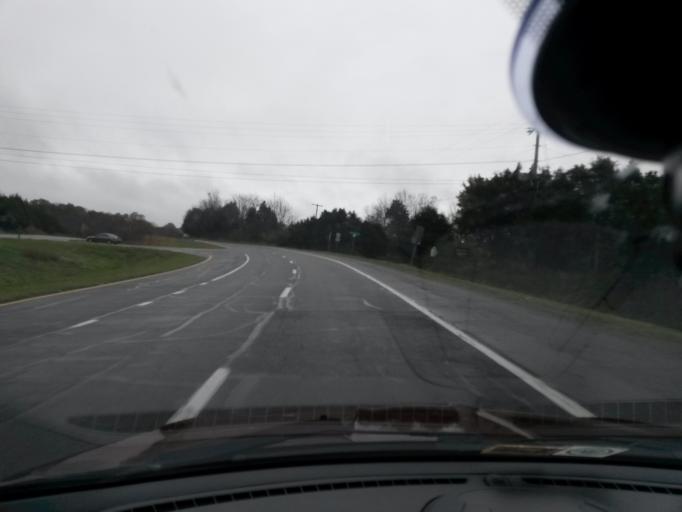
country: US
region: Virginia
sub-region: Botetourt County
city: Fincastle
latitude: 37.5194
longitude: -79.8784
